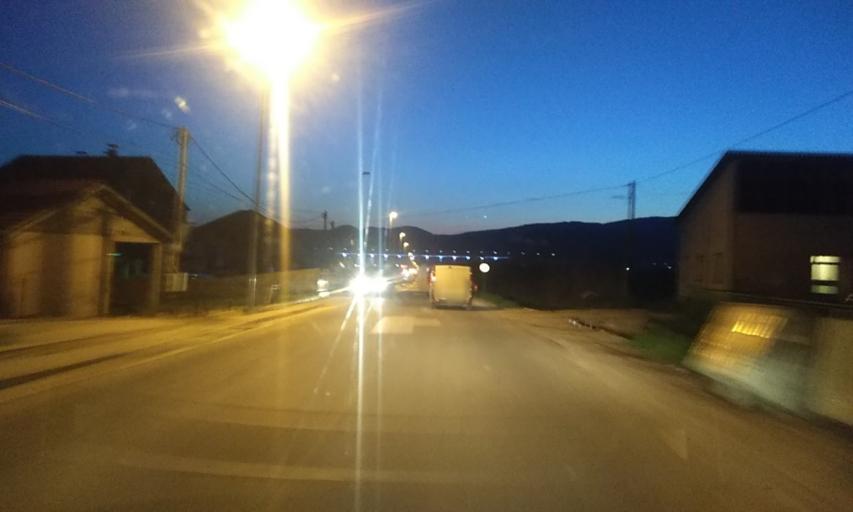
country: RS
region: Central Serbia
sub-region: Pcinjski Okrug
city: Vladicin Han
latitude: 42.7108
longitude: 22.1000
